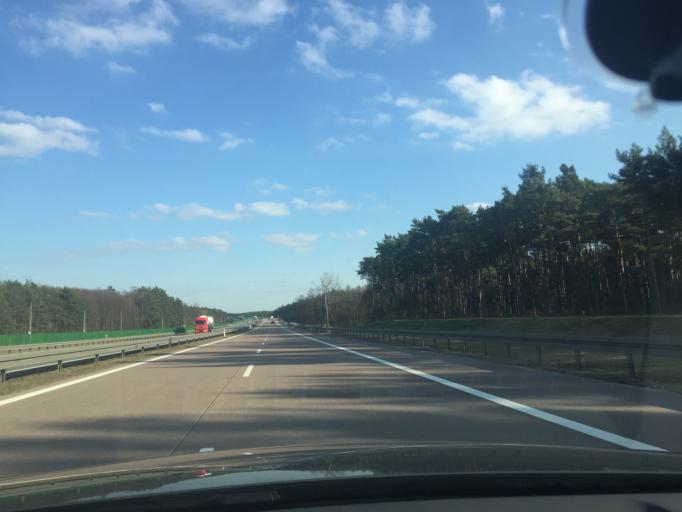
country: PL
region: Lubusz
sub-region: Powiat slubicki
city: Rzepin
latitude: 52.3309
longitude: 14.8259
